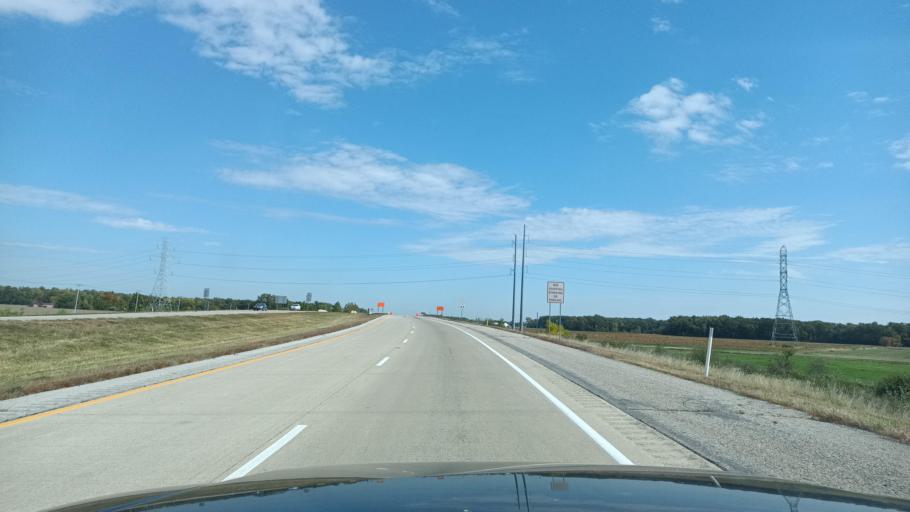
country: US
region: Indiana
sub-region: Allen County
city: New Haven
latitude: 41.0886
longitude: -84.9847
